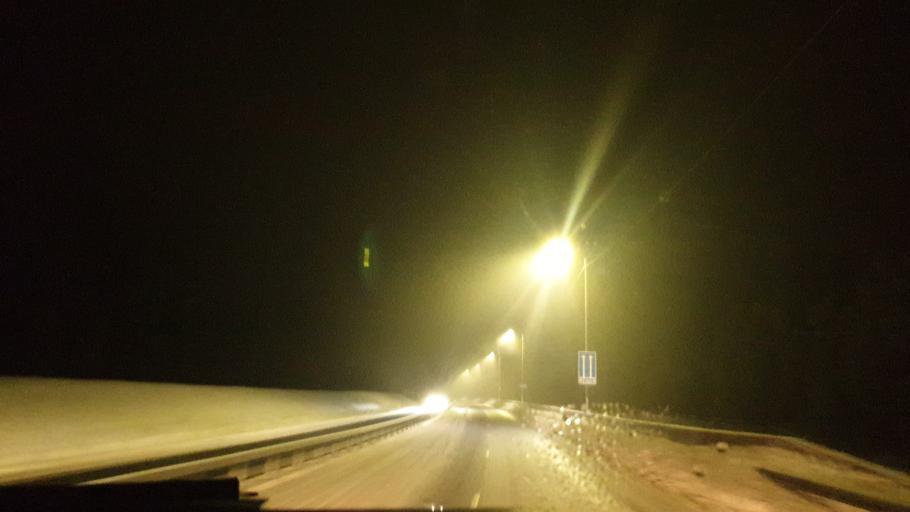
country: FI
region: Northern Ostrobothnia
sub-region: Oulunkaari
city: Kuivaniemi
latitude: 65.5848
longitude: 25.1976
